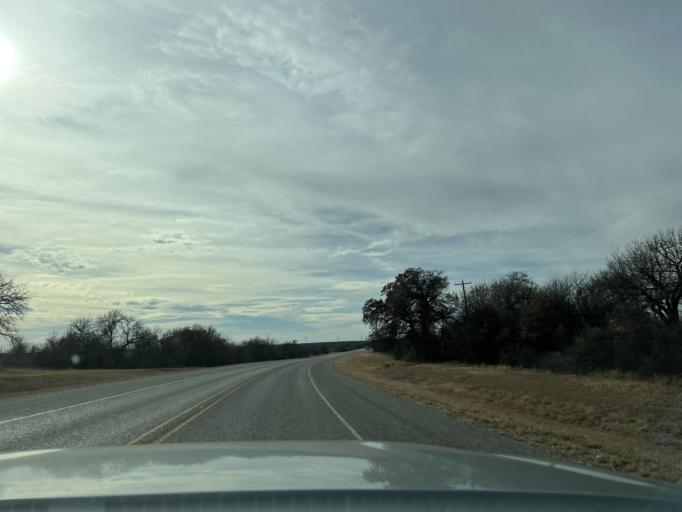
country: US
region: Texas
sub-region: Jones County
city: Stamford
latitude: 32.7576
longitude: -99.6069
